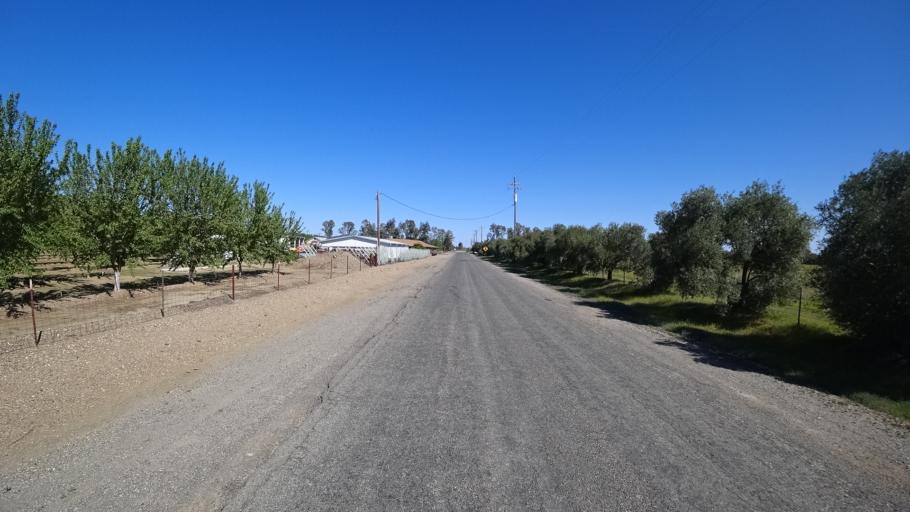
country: US
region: California
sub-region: Glenn County
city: Orland
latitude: 39.7238
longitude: -122.2112
